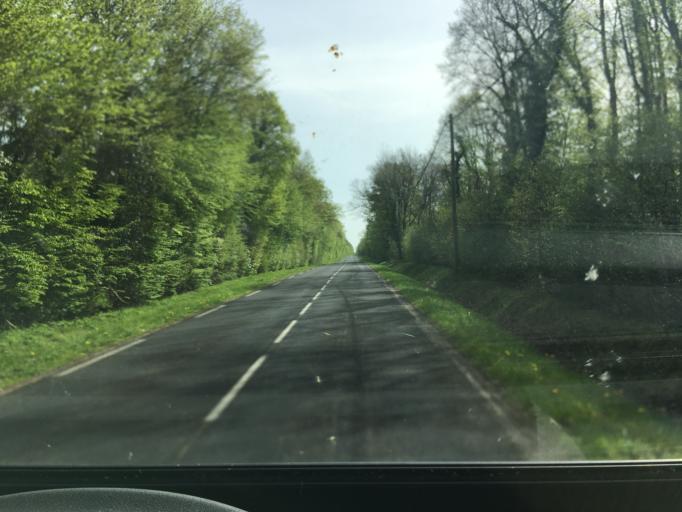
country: FR
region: Lorraine
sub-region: Departement de Meurthe-et-Moselle
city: Gondreville
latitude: 48.6637
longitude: 5.9955
